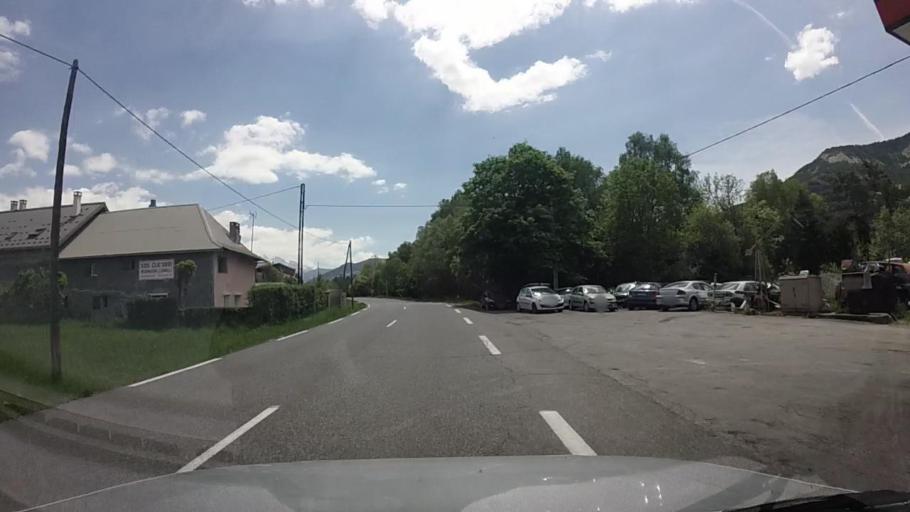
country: FR
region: Provence-Alpes-Cote d'Azur
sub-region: Departement des Alpes-de-Haute-Provence
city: Seyne-les-Alpes
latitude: 44.3671
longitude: 6.3195
